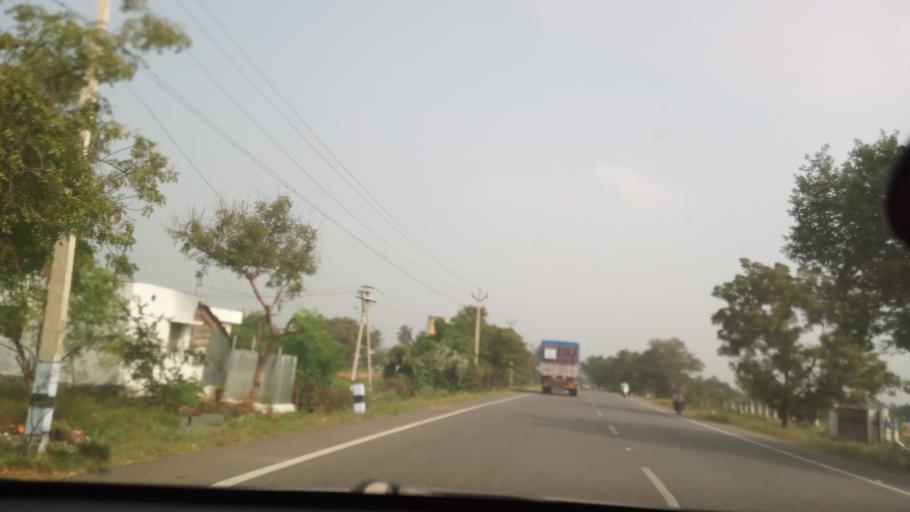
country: IN
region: Tamil Nadu
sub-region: Erode
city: Punjai Puliyampatti
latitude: 11.3713
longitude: 77.1710
